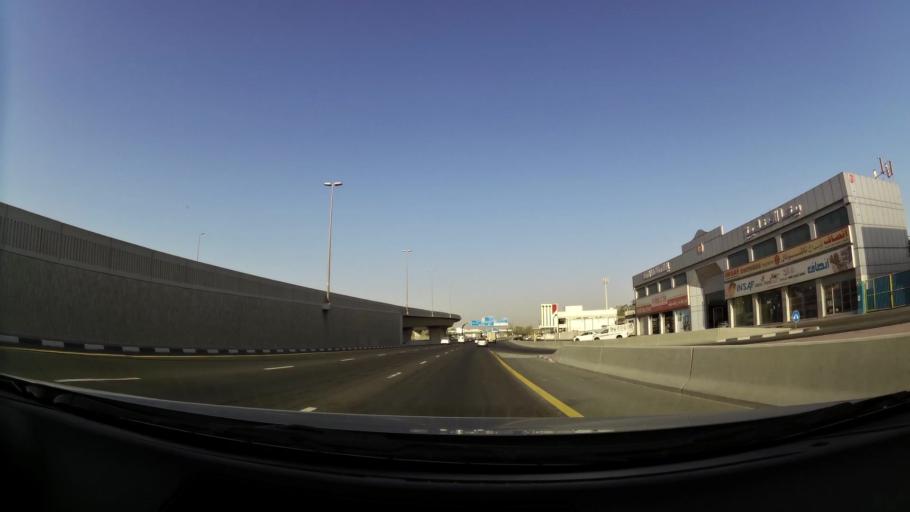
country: AE
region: Ash Shariqah
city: Sharjah
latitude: 25.1856
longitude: 55.3661
